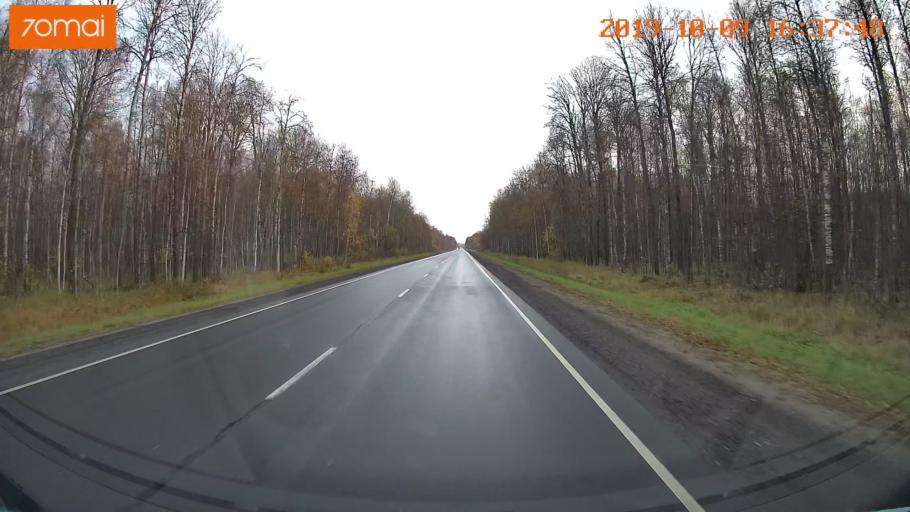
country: RU
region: Kostroma
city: Volgorechensk
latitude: 57.5214
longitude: 41.0292
